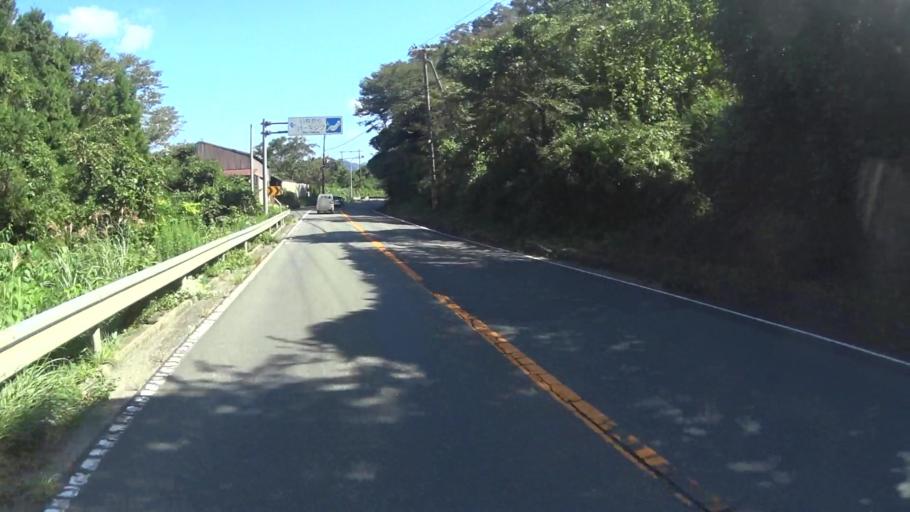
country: JP
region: Kyoto
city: Ayabe
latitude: 35.2376
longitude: 135.4136
